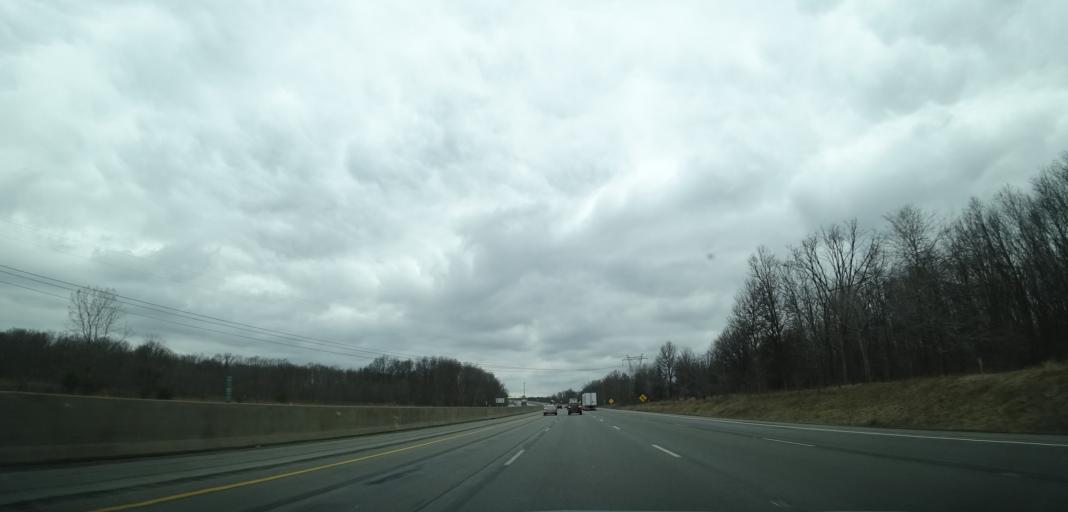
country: US
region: Ohio
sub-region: Trumbull County
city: Lordstown
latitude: 41.1210
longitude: -80.8466
